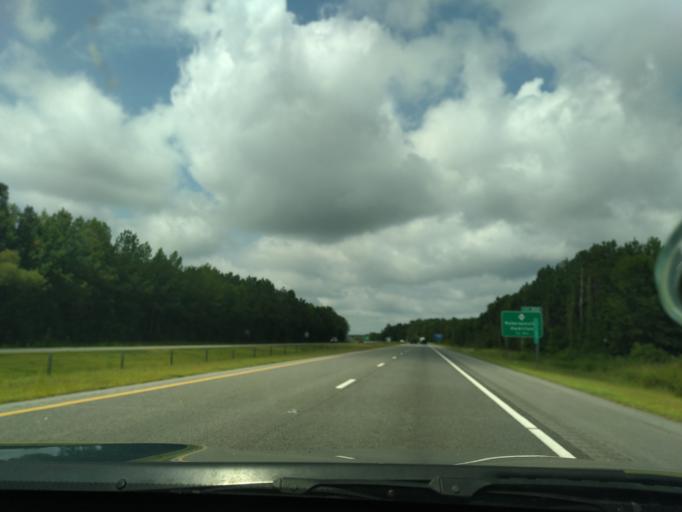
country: US
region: North Carolina
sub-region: Martin County
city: Robersonville
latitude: 35.8410
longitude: -77.2359
